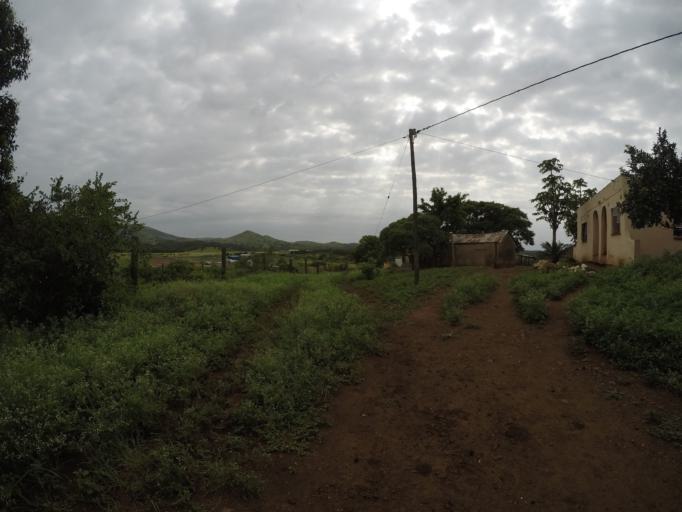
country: ZA
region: KwaZulu-Natal
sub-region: uThungulu District Municipality
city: Empangeni
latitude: -28.6394
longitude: 31.9095
